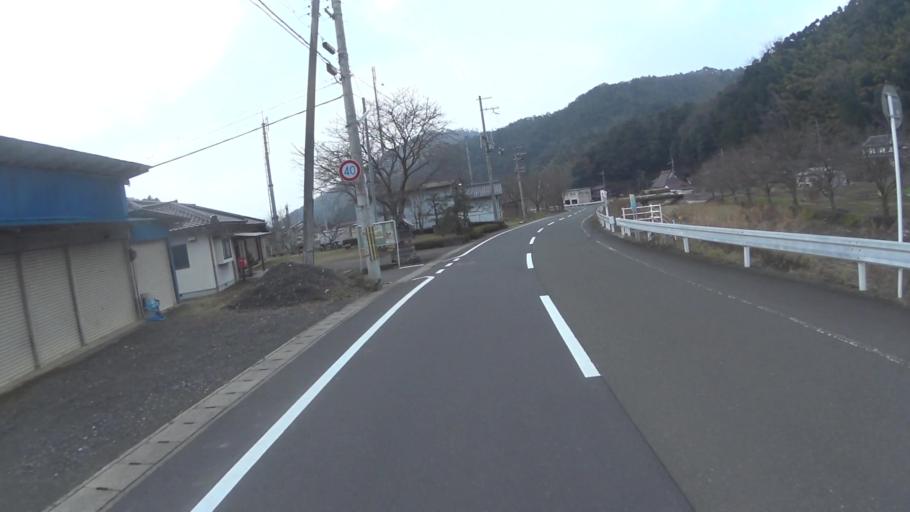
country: JP
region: Kyoto
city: Maizuru
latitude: 35.4446
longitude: 135.4396
